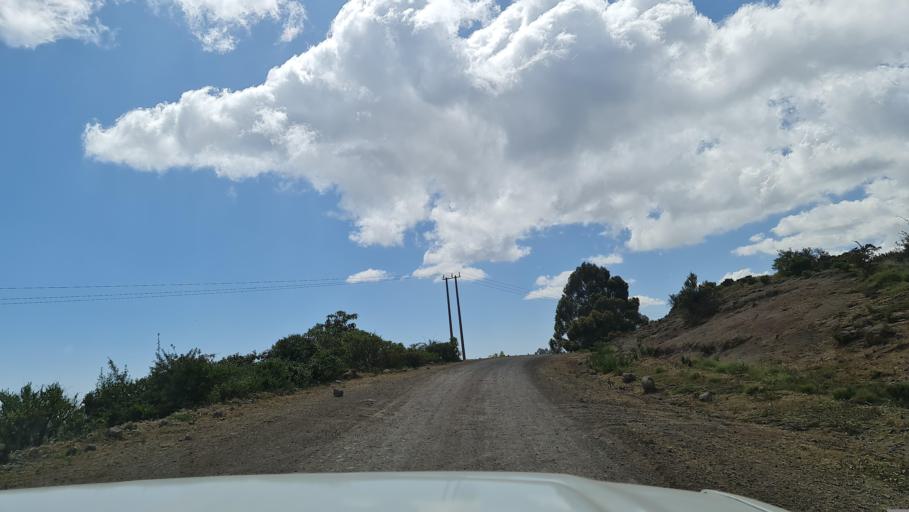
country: ET
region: Amhara
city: Debark'
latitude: 13.2196
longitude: 38.0123
